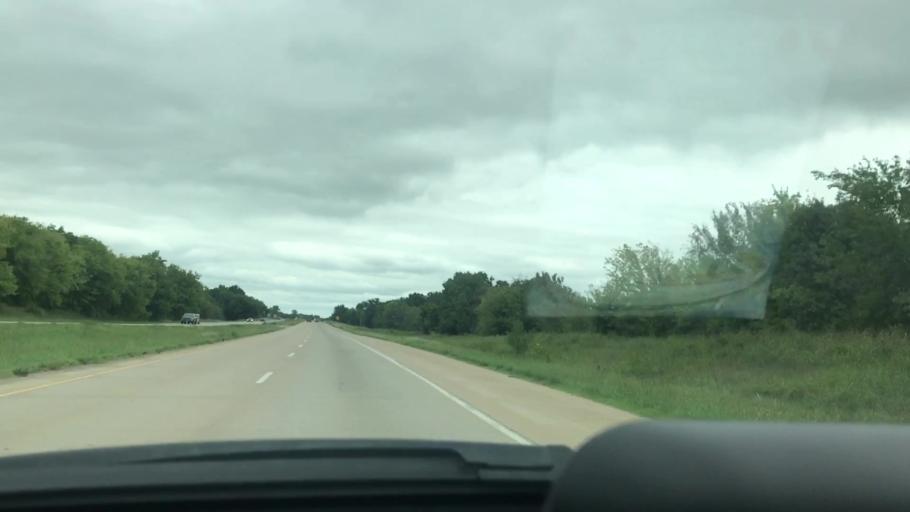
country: US
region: Oklahoma
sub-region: Mayes County
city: Chouteau
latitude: 36.2022
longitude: -95.3408
